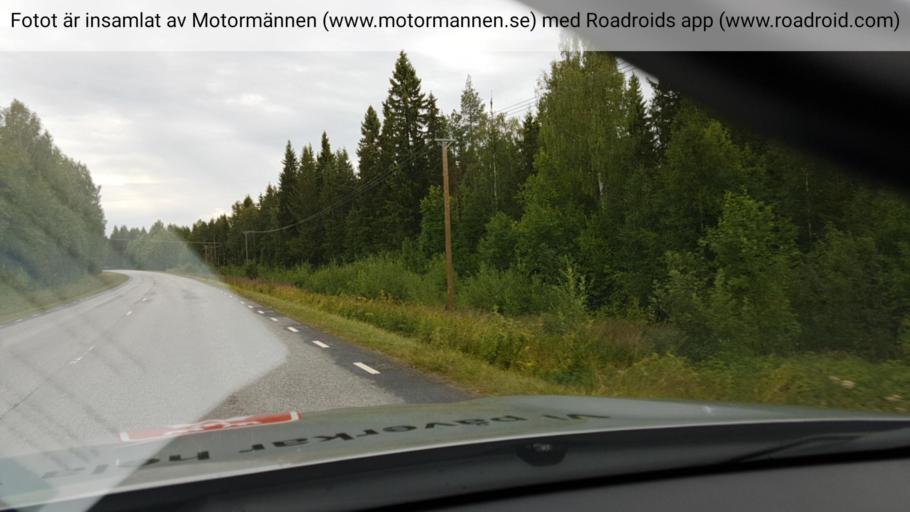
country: SE
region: Norrbotten
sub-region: Bodens Kommun
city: Boden
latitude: 65.8033
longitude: 21.6574
